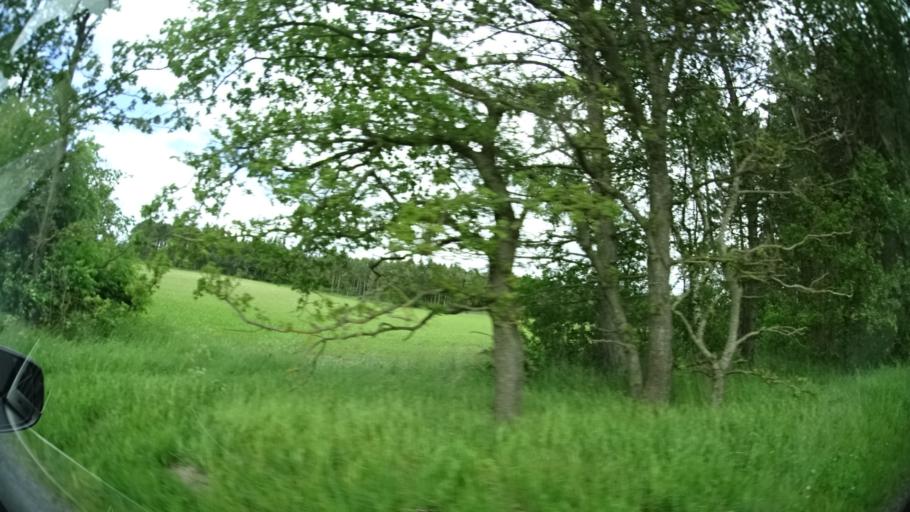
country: DK
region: Central Jutland
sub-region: Norddjurs Kommune
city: Grenaa
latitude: 56.5085
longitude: 10.7320
